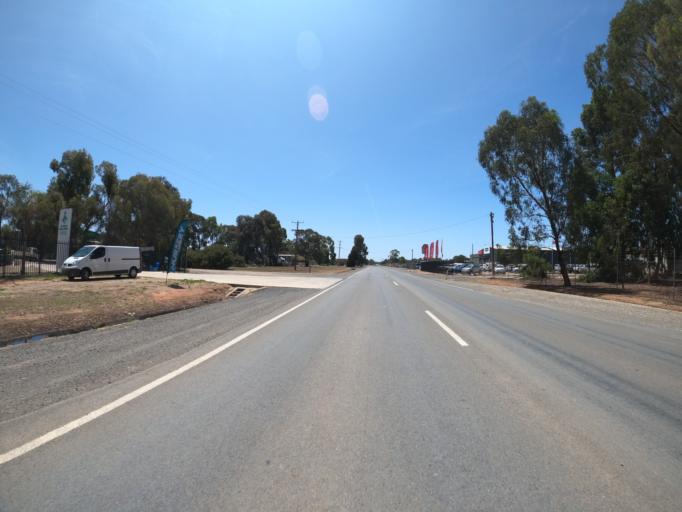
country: AU
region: Victoria
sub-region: Moira
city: Yarrawonga
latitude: -36.0318
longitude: 145.9955
